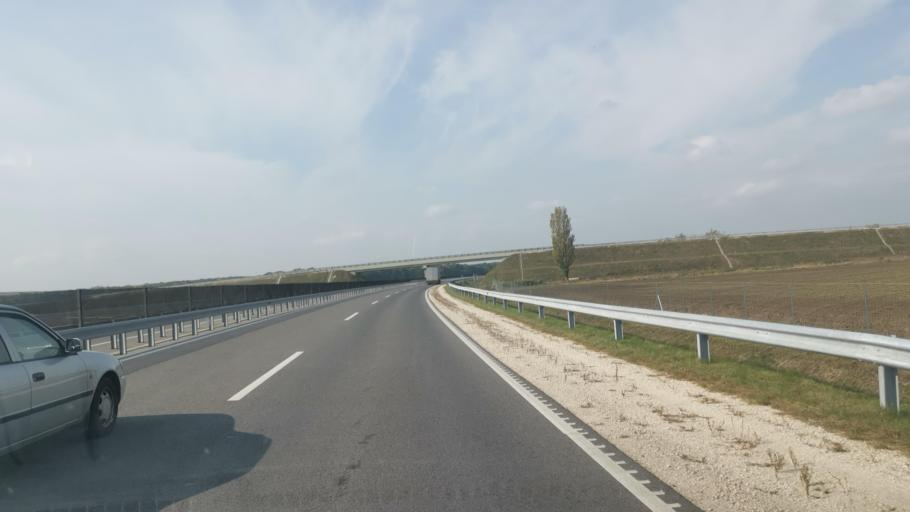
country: HU
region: Gyor-Moson-Sopron
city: Kapuvar
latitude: 47.5617
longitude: 17.0717
